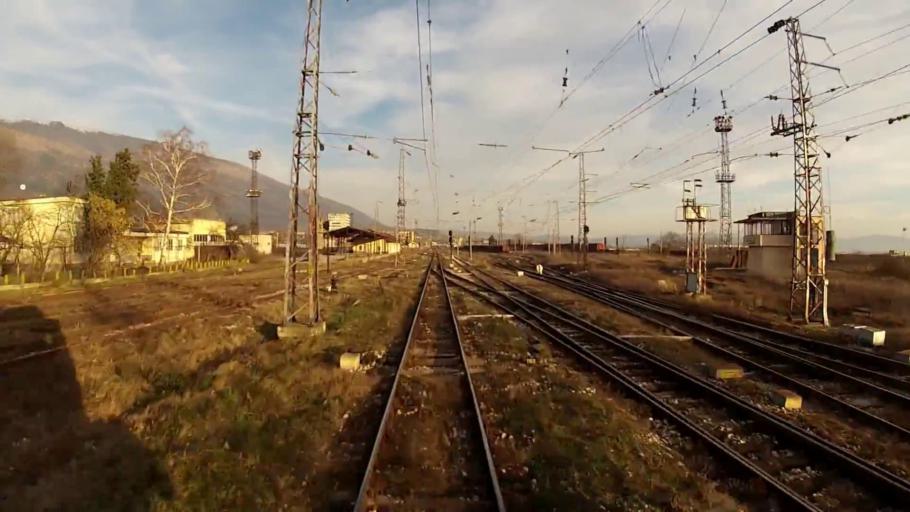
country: BG
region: Plovdiv
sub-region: Obshtina Karlovo
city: Karlovo
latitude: 42.6316
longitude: 24.7931
